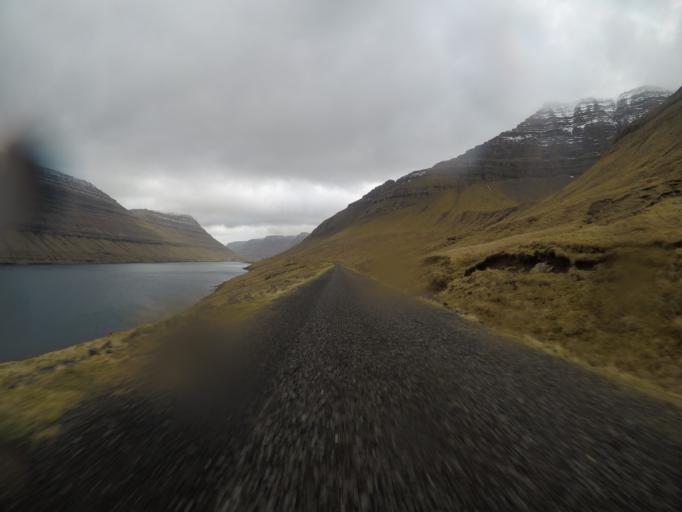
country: FO
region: Nordoyar
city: Klaksvik
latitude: 62.3213
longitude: -6.5599
